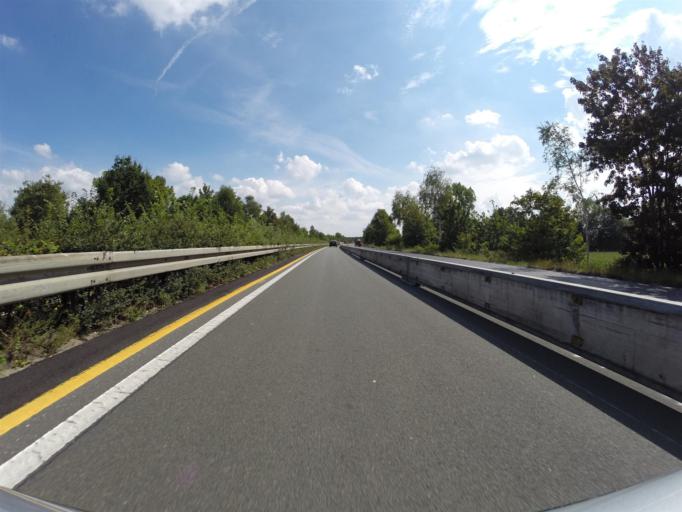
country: DE
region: North Rhine-Westphalia
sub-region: Regierungsbezirk Detmold
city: Hovelhof
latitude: 51.8179
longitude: 8.7011
